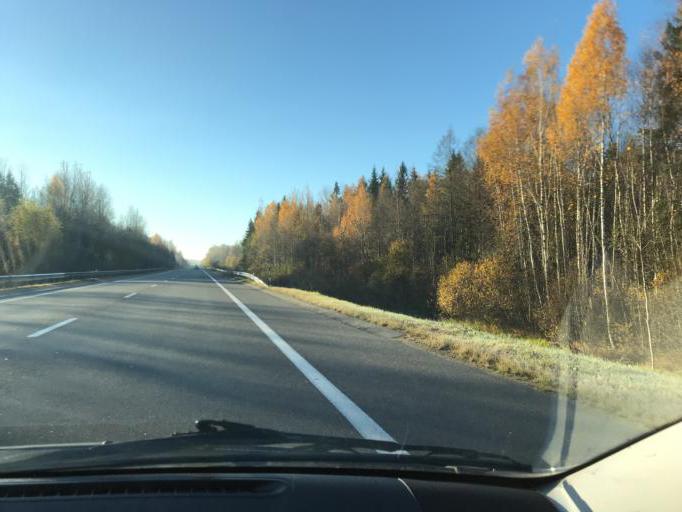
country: BY
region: Vitebsk
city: Vitebsk
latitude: 54.9867
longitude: 30.3434
